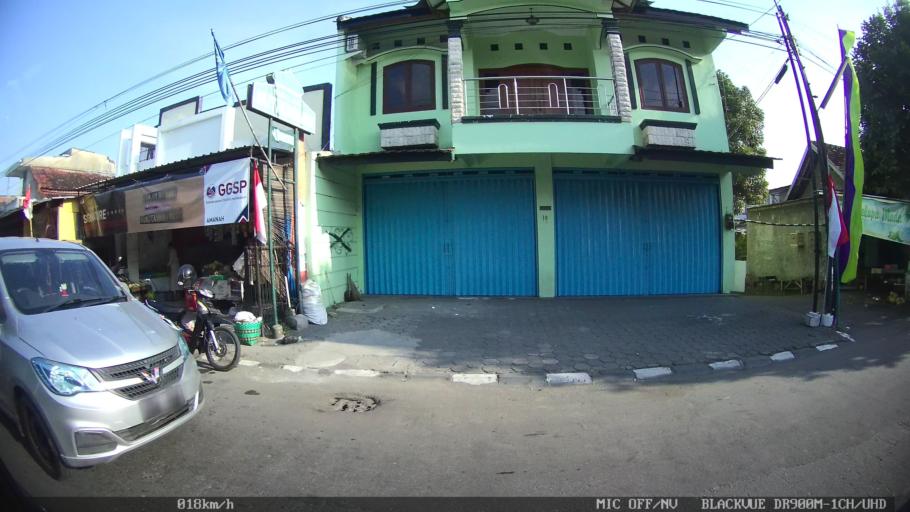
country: ID
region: Daerah Istimewa Yogyakarta
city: Yogyakarta
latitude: -7.8252
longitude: 110.3839
